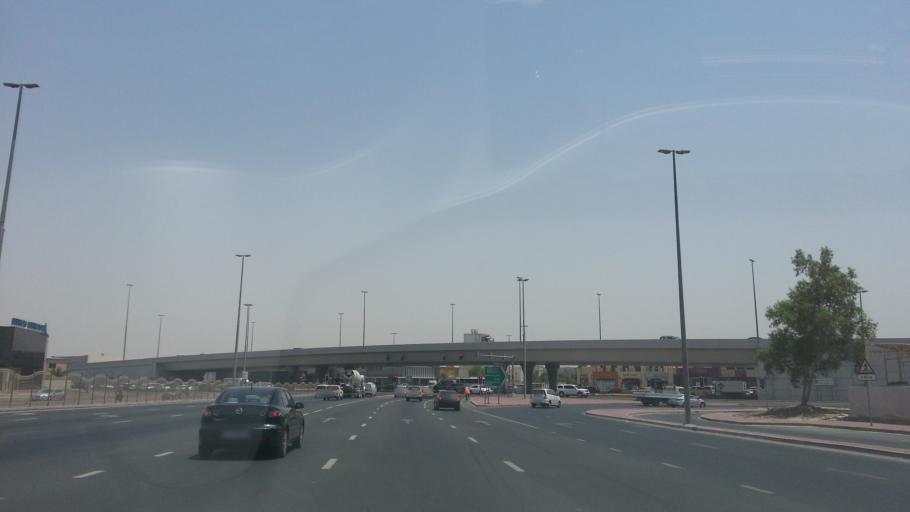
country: AE
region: Dubai
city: Dubai
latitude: 25.1126
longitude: 55.2197
